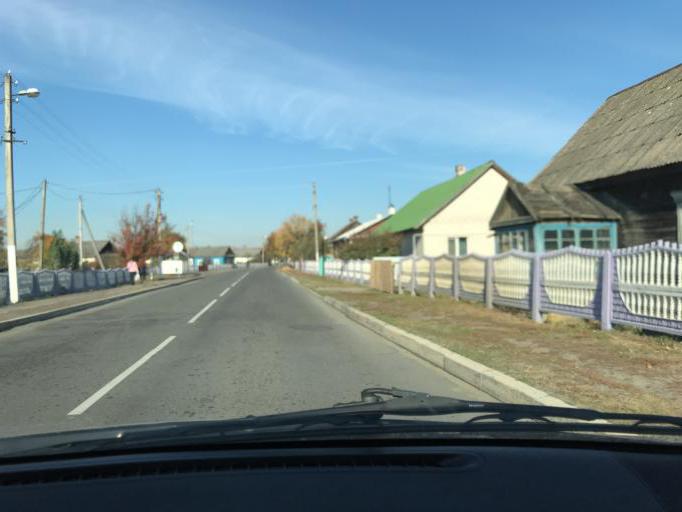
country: BY
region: Brest
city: Mikashevichy
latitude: 52.2239
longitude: 27.4627
